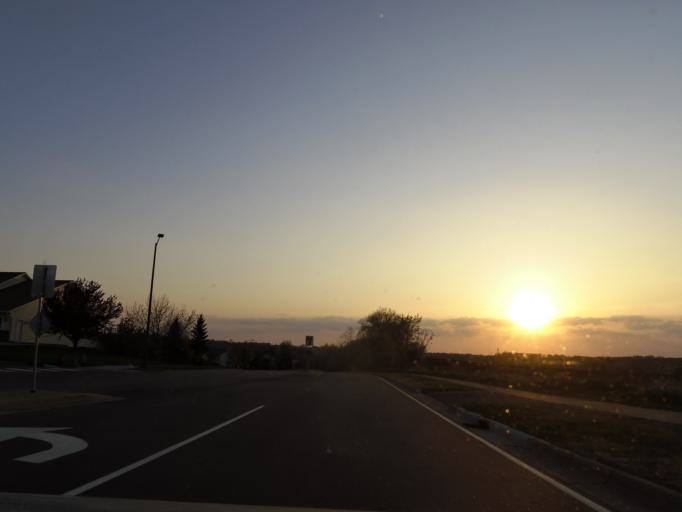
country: US
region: Minnesota
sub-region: Scott County
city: Prior Lake
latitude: 44.7395
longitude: -93.4326
